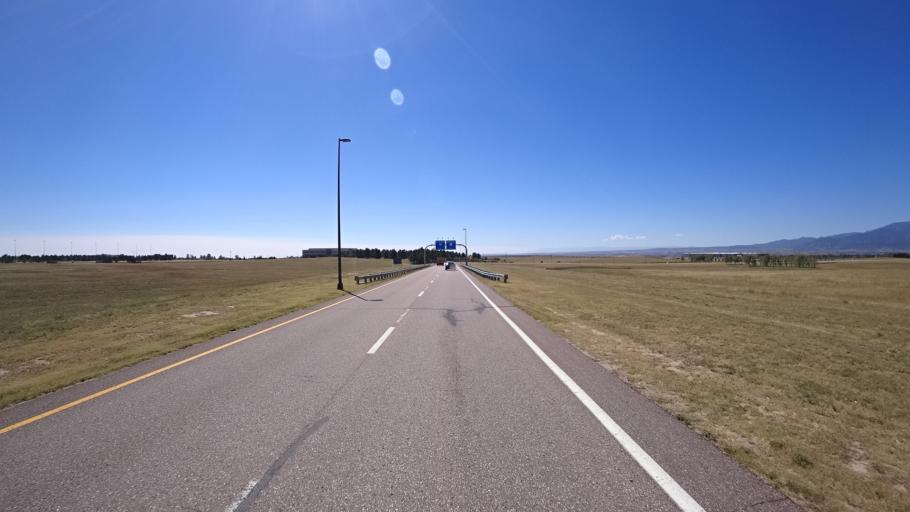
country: US
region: Colorado
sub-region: El Paso County
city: Security-Widefield
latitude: 38.7854
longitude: -104.7043
